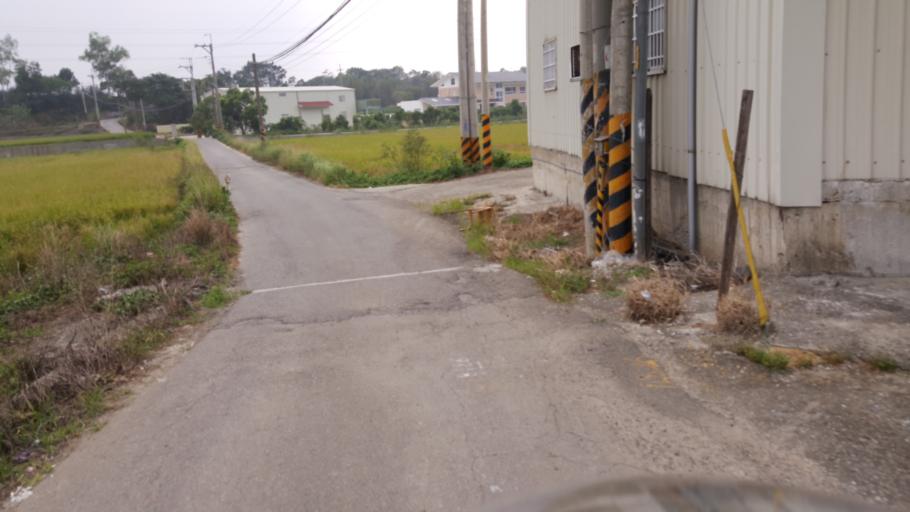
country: TW
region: Taiwan
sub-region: Hsinchu
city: Hsinchu
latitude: 24.7062
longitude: 120.9450
